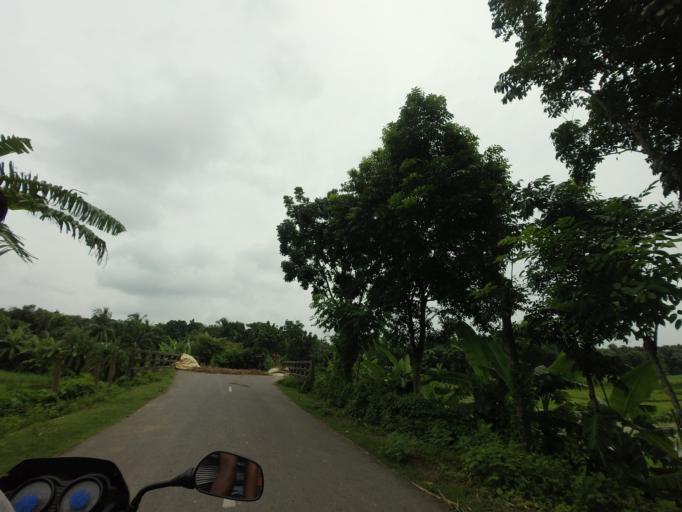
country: BD
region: Khulna
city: Kalia
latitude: 23.1109
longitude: 89.6468
